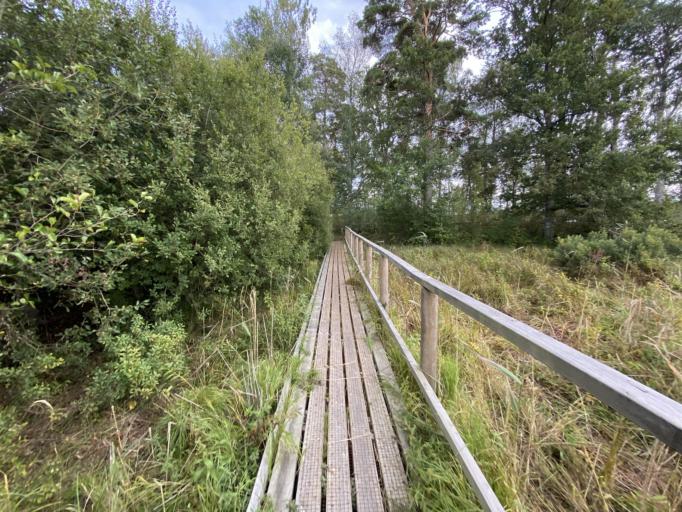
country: SE
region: Skane
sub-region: Hassleholms Kommun
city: Hastveda
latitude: 56.3613
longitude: 13.8859
